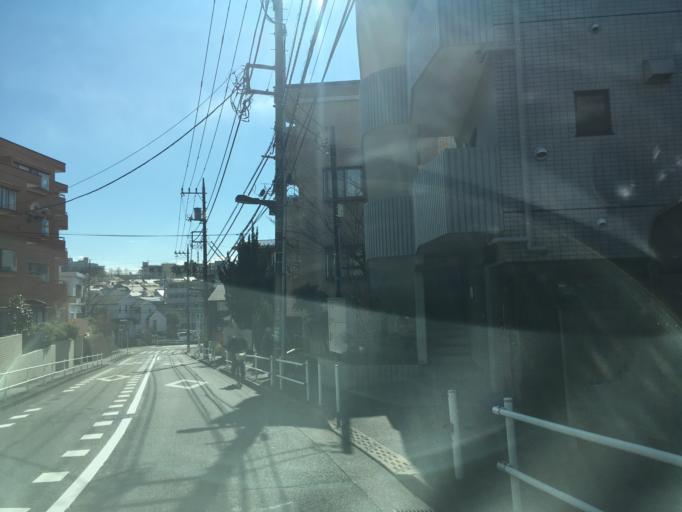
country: JP
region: Tokyo
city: Hino
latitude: 35.6348
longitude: 139.4524
